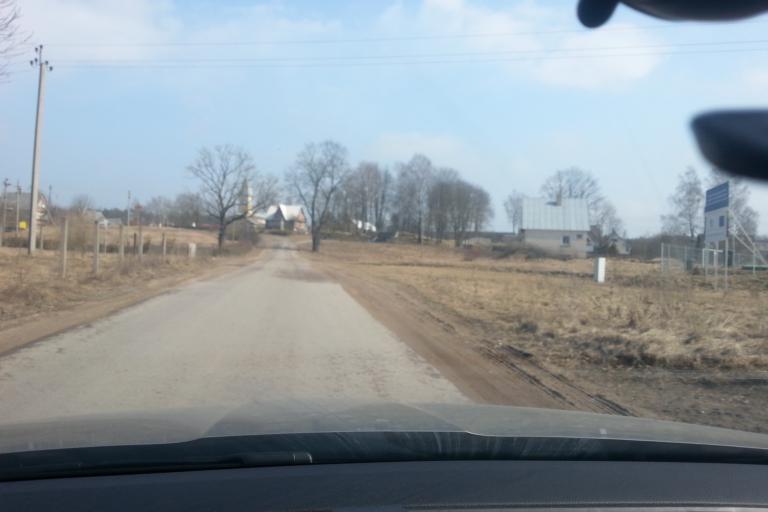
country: LT
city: Trakai
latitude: 54.5004
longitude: 24.9827
